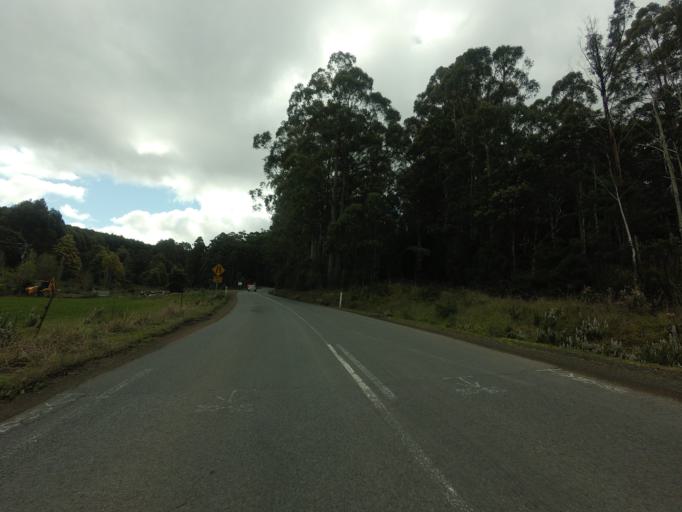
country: AU
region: Tasmania
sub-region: Huon Valley
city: Cygnet
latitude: -43.2673
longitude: 147.0111
